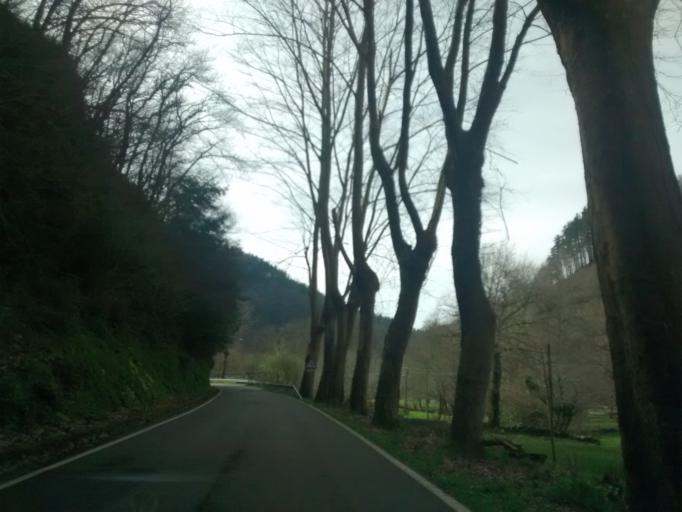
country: ES
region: Cantabria
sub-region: Provincia de Cantabria
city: San Pedro del Romeral
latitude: 43.1676
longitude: -3.8516
